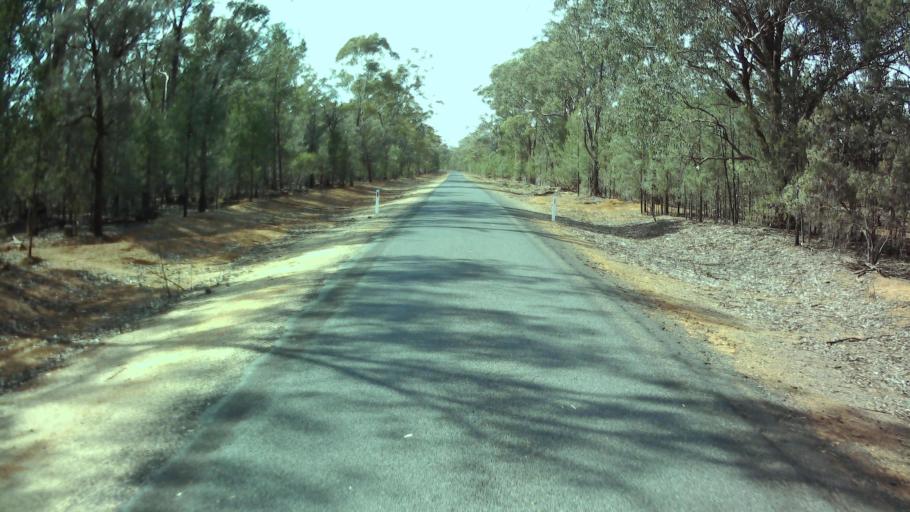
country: AU
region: New South Wales
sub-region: Weddin
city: Grenfell
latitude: -33.7191
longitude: 148.0272
